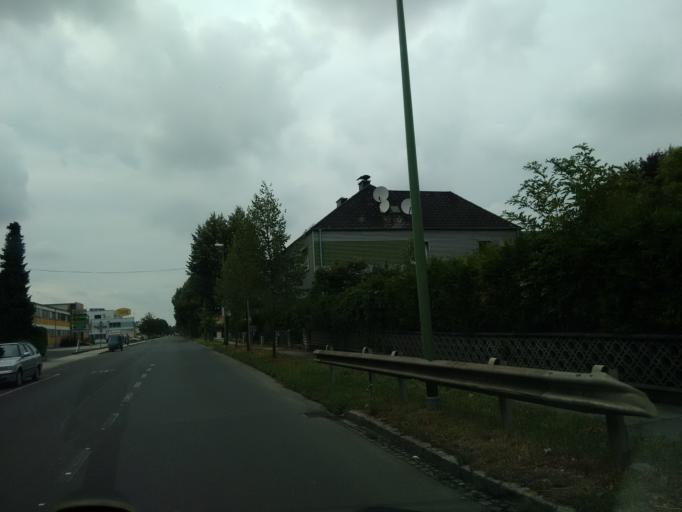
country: AT
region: Upper Austria
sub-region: Wels Stadt
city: Wels
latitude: 48.1627
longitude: 14.0608
